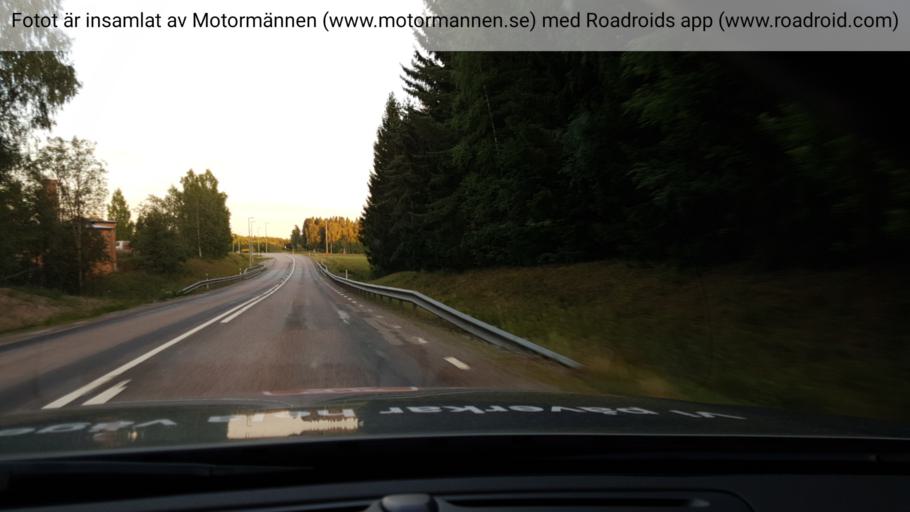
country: SE
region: OErebro
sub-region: Karlskoga Kommun
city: Karlskoga
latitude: 59.3881
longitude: 14.4726
